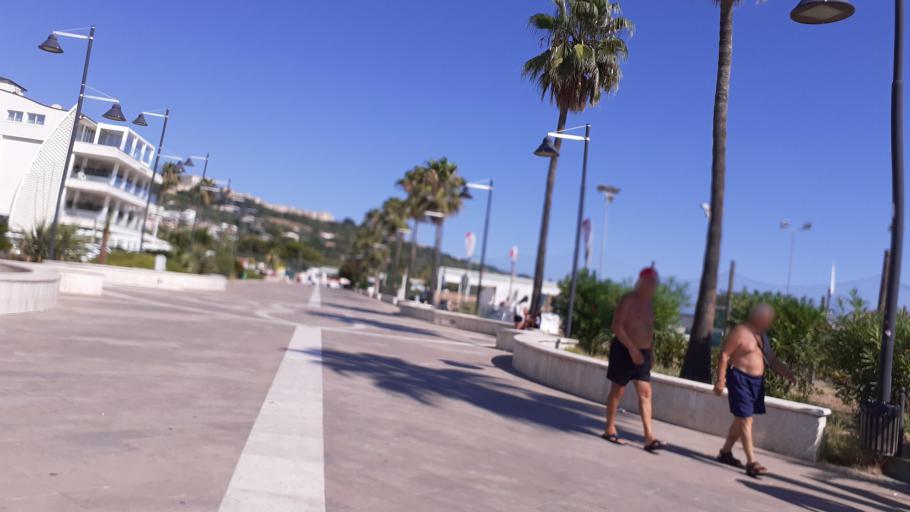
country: IT
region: Abruzzo
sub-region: Provincia di Chieti
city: Marina di Vasto
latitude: 42.1012
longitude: 14.7199
